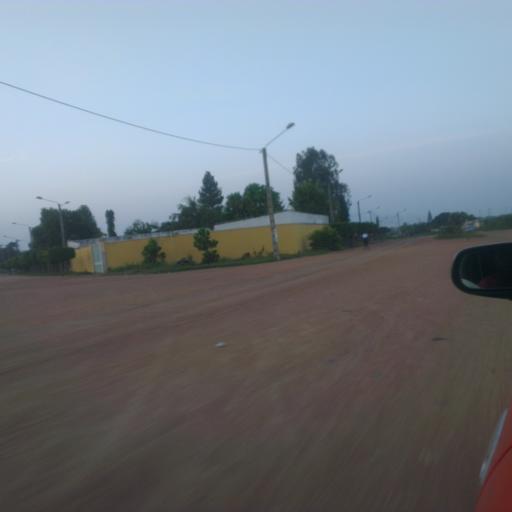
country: CI
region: Vallee du Bandama
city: Bouake
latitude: 7.6904
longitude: -5.0577
